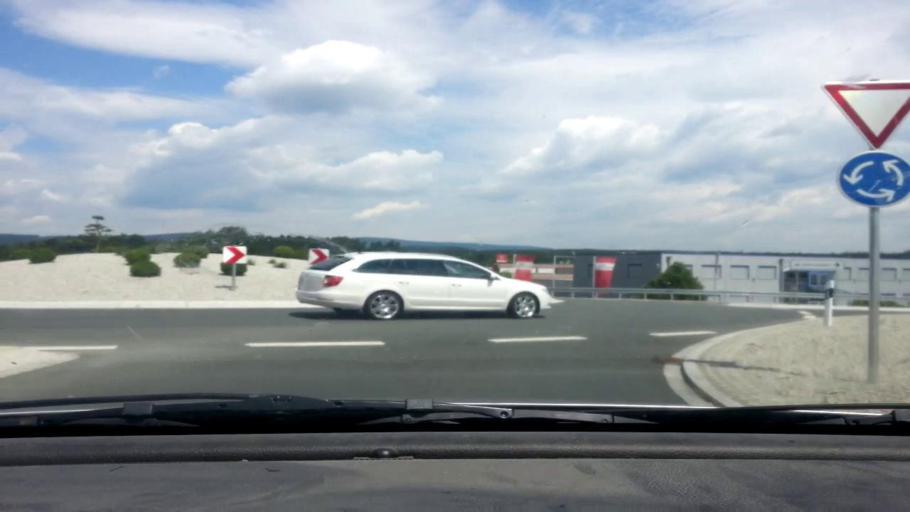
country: DE
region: Bavaria
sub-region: Upper Palatinate
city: Erbendorf
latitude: 49.8321
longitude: 12.0626
